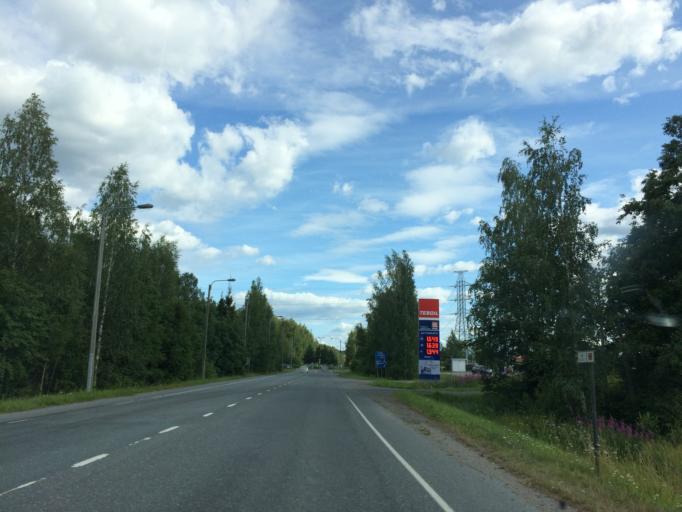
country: FI
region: Haeme
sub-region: Haemeenlinna
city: Haemeenlinna
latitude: 60.9977
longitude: 24.4911
